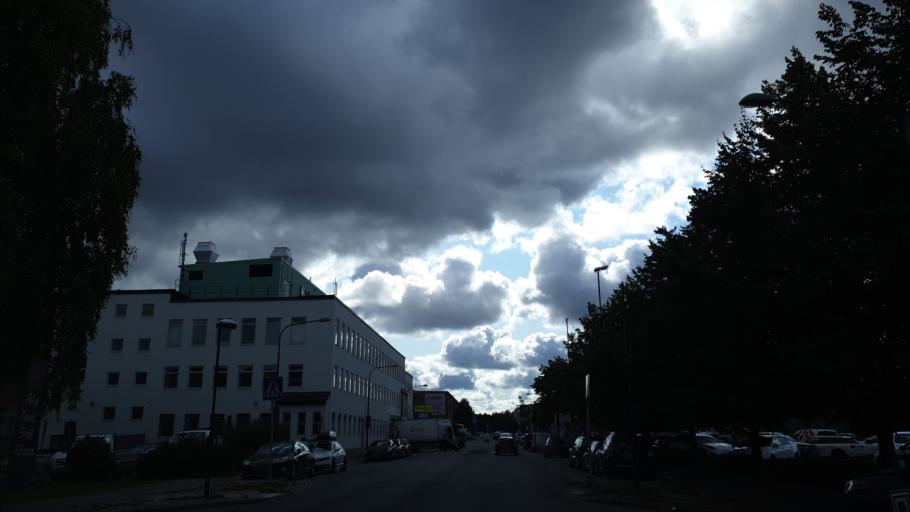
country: SE
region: Stockholm
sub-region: Sundbybergs Kommun
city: Sundbyberg
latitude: 59.3514
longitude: 17.9589
